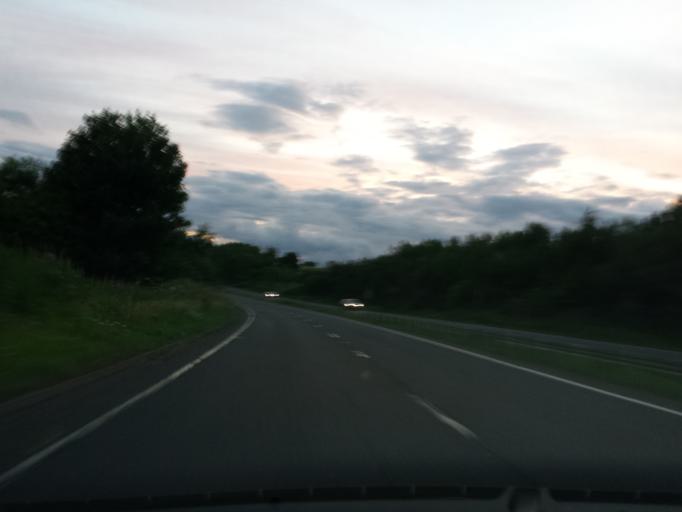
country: GB
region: Scotland
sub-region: The Scottish Borders
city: Chirnside
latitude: 55.8575
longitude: -2.2144
